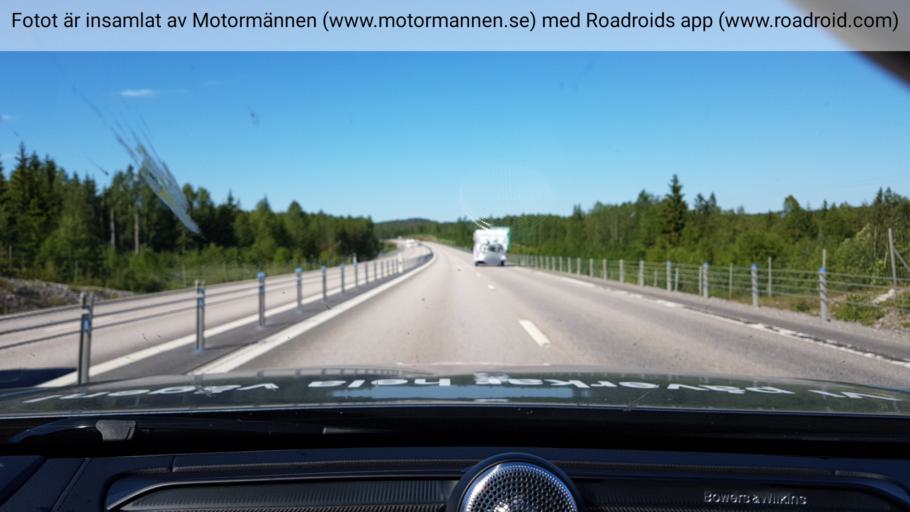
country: SE
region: Gaevleborg
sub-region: Hudiksvalls Kommun
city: Iggesund
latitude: 61.6330
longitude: 17.0135
